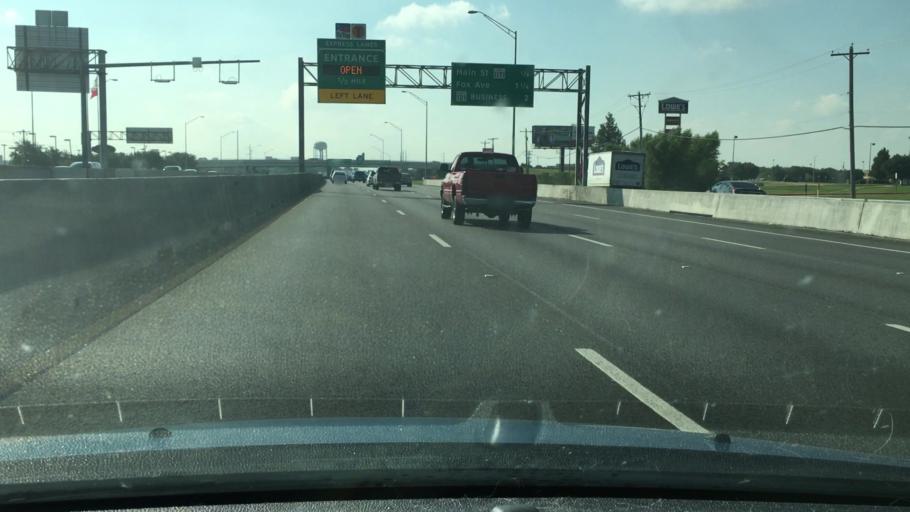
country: US
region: Texas
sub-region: Denton County
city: Lewisville
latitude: 33.0593
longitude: -97.0130
